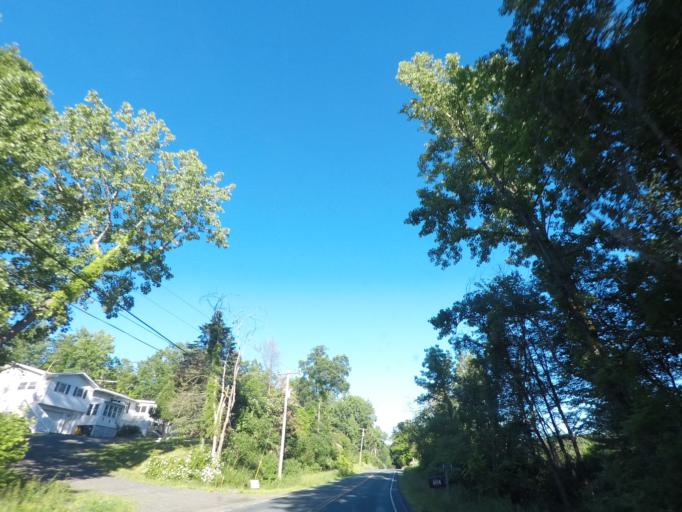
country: US
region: New York
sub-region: Rensselaer County
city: Averill Park
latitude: 42.5931
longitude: -73.5880
